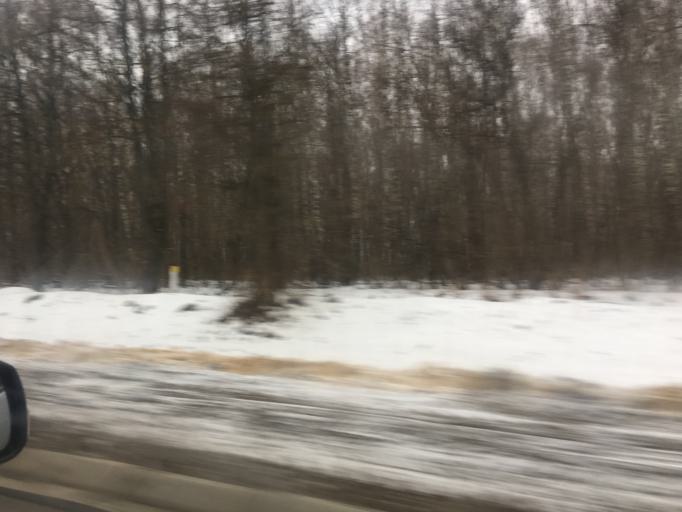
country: RU
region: Tula
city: Pervomayskiy
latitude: 54.0645
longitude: 37.5342
